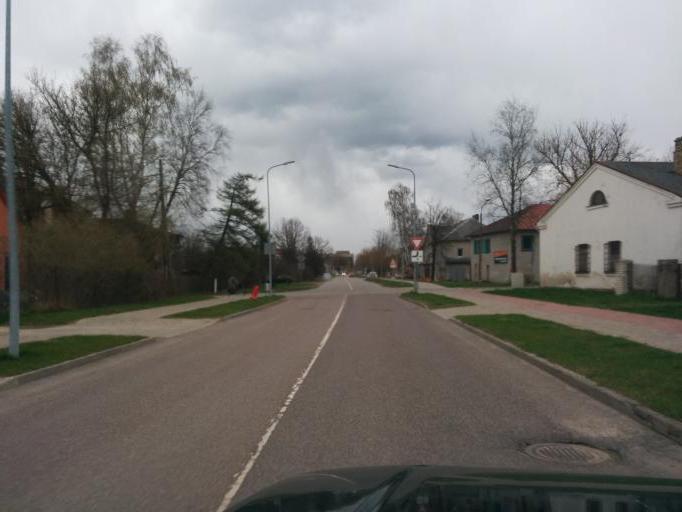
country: LV
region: Jelgava
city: Jelgava
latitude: 56.6529
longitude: 23.7457
